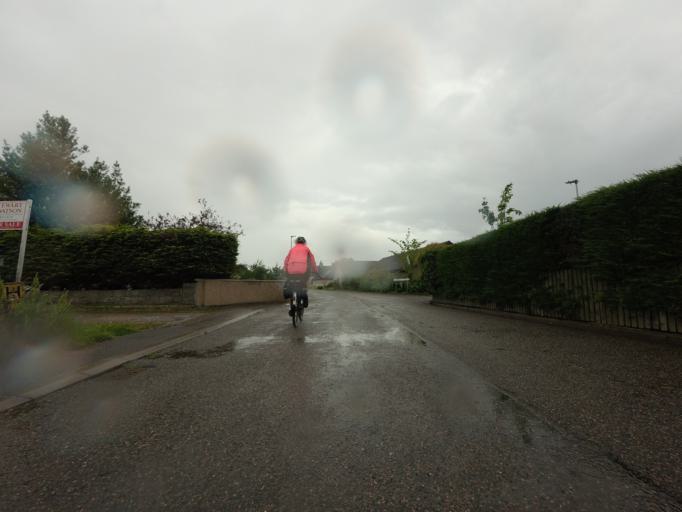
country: GB
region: Scotland
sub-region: Moray
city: Fochabers
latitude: 57.6614
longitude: -3.0733
